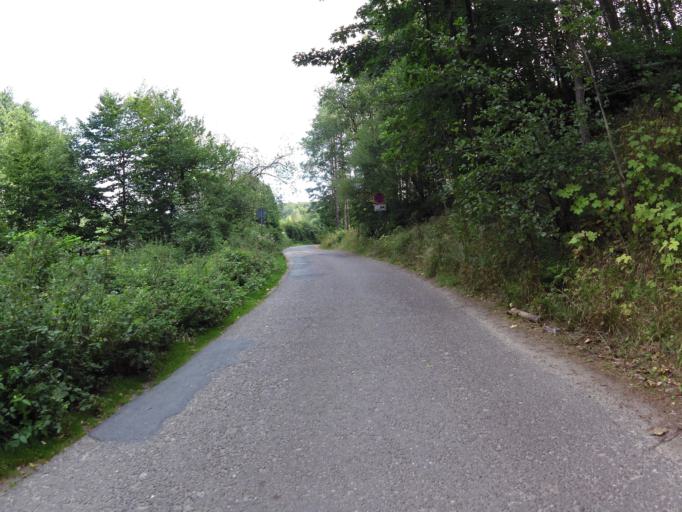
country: DE
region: Mecklenburg-Vorpommern
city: Seebad Bansin
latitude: 53.9860
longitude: 14.1106
